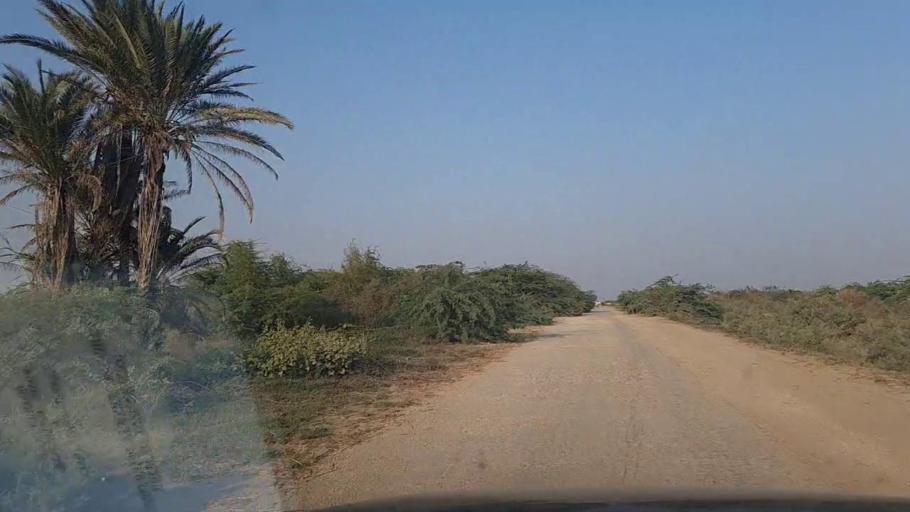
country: PK
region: Sindh
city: Keti Bandar
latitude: 24.2560
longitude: 67.5386
